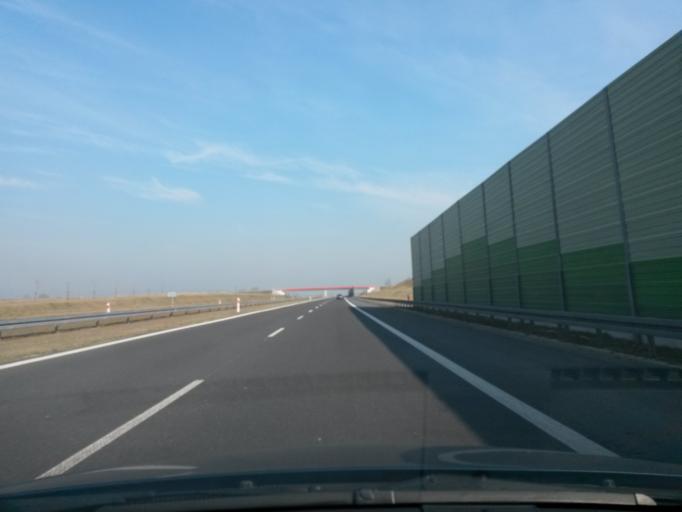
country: PL
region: Lodz Voivodeship
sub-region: Powiat kutnowski
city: Krzyzanow
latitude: 52.1528
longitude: 19.4820
